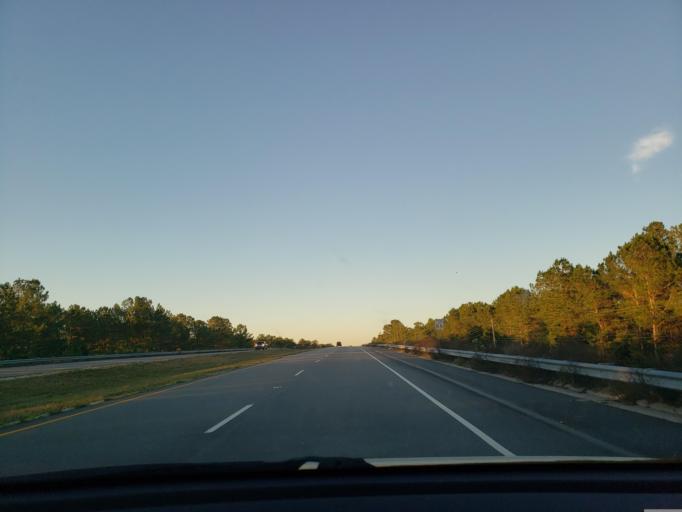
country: US
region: North Carolina
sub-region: Onslow County
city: Sneads Ferry
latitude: 34.5929
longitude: -77.4802
